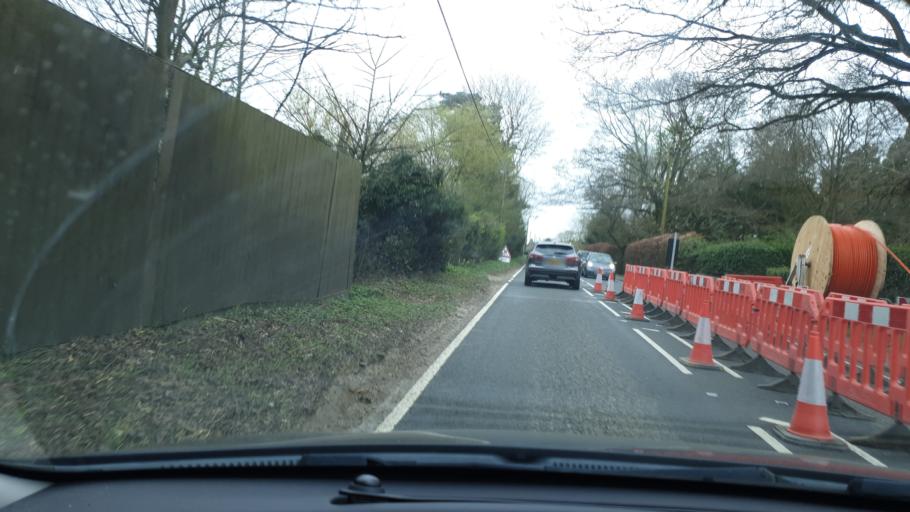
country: GB
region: England
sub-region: Essex
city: Great Horkesley
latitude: 51.9434
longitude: 0.8756
